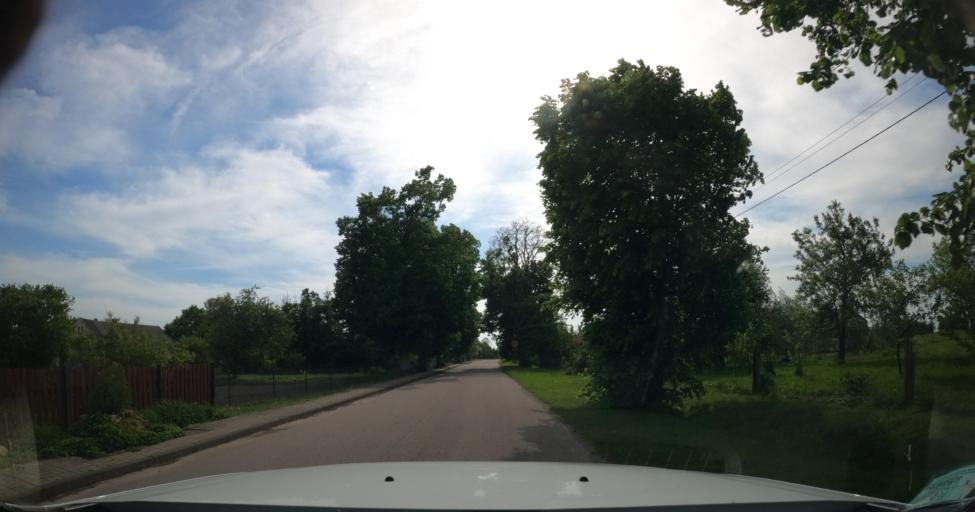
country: PL
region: Warmian-Masurian Voivodeship
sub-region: Powiat lidzbarski
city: Orneta
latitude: 54.0521
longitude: 20.1563
